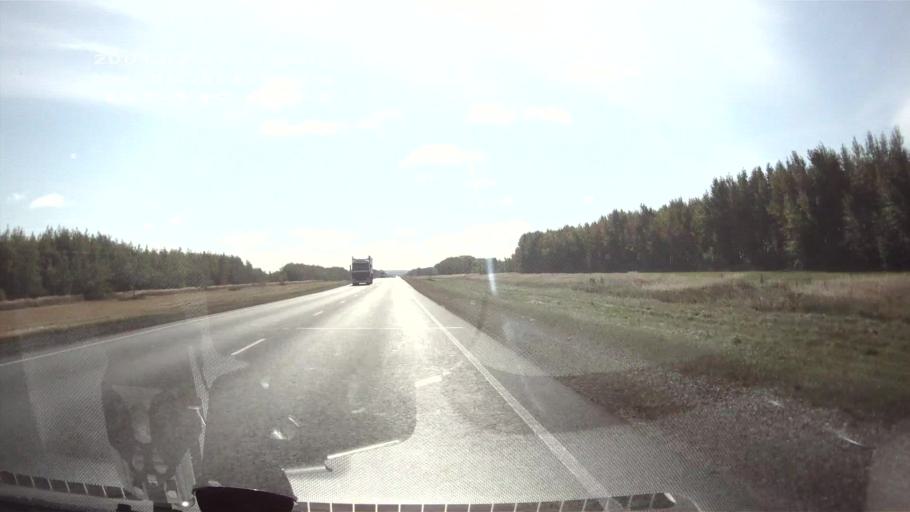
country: RU
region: Ulyanovsk
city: Tsil'na
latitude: 54.5621
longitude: 47.9234
